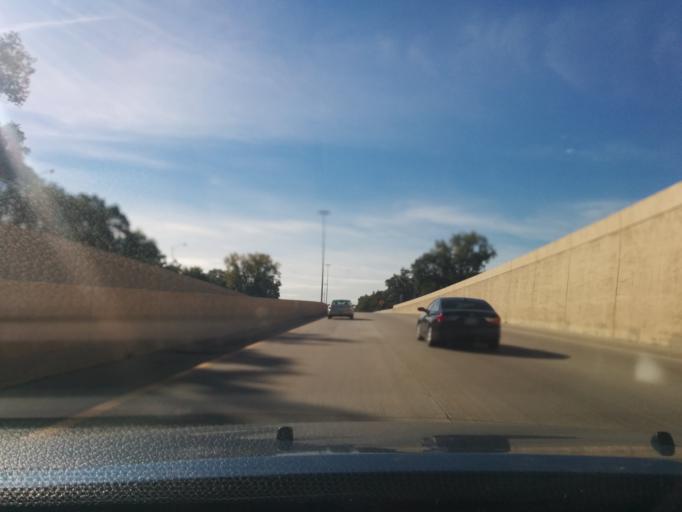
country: US
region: Michigan
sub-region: Oakland County
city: Southfield
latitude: 42.4430
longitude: -83.2199
